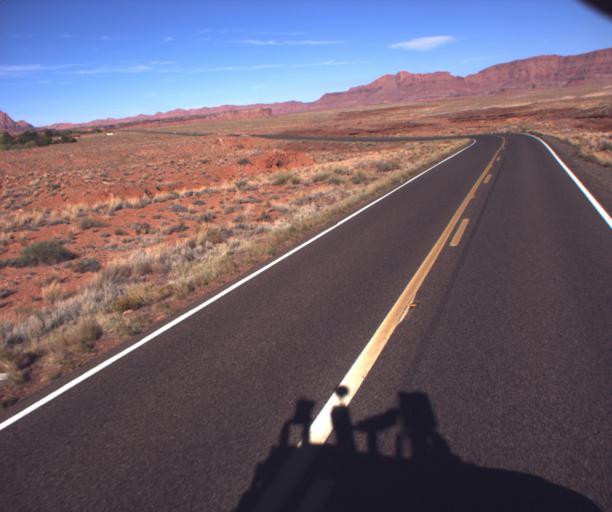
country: US
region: Arizona
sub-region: Coconino County
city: Page
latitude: 36.7801
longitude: -111.6911
